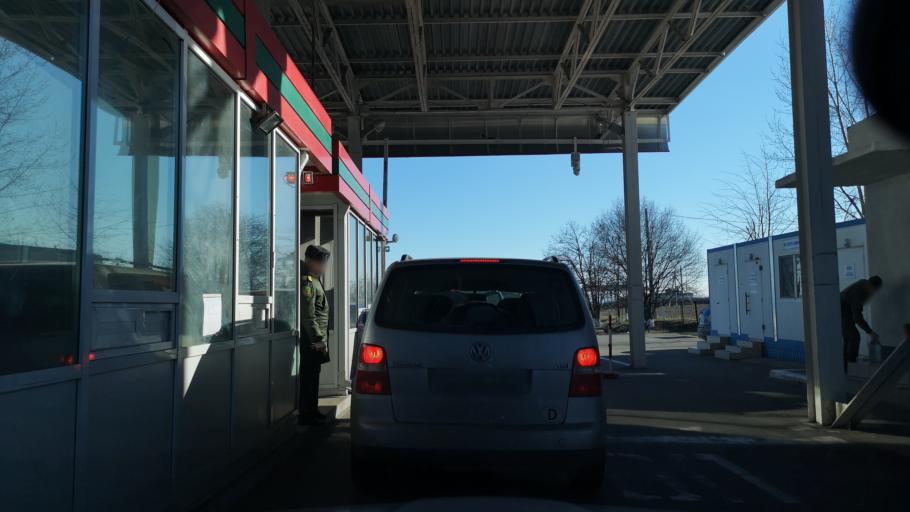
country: MD
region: Anenii Noi
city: Varnita
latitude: 46.8576
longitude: 29.4398
